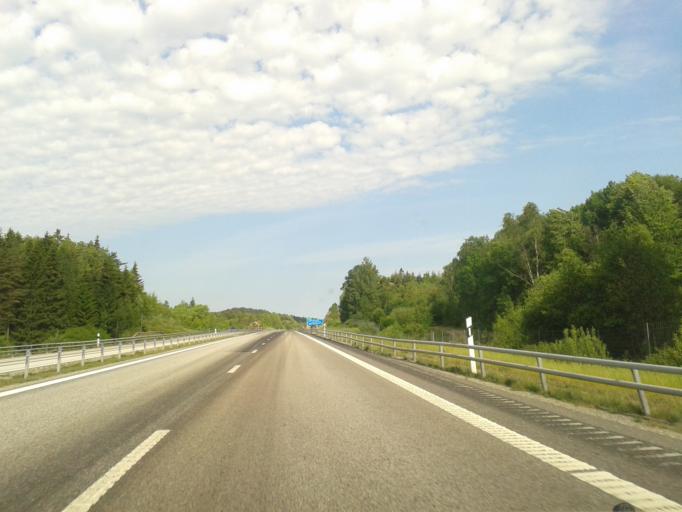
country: SE
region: Vaestra Goetaland
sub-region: Lysekils Kommun
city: Brastad
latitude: 58.5550
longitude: 11.4977
